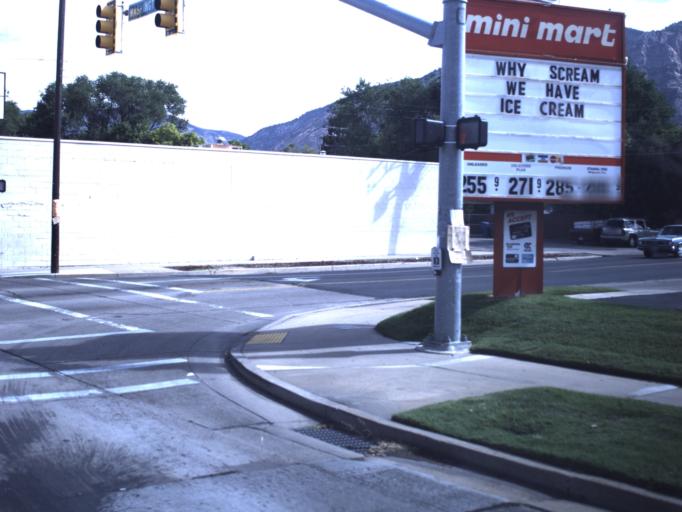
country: US
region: Utah
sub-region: Weber County
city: Ogden
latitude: 41.2515
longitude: -111.9697
